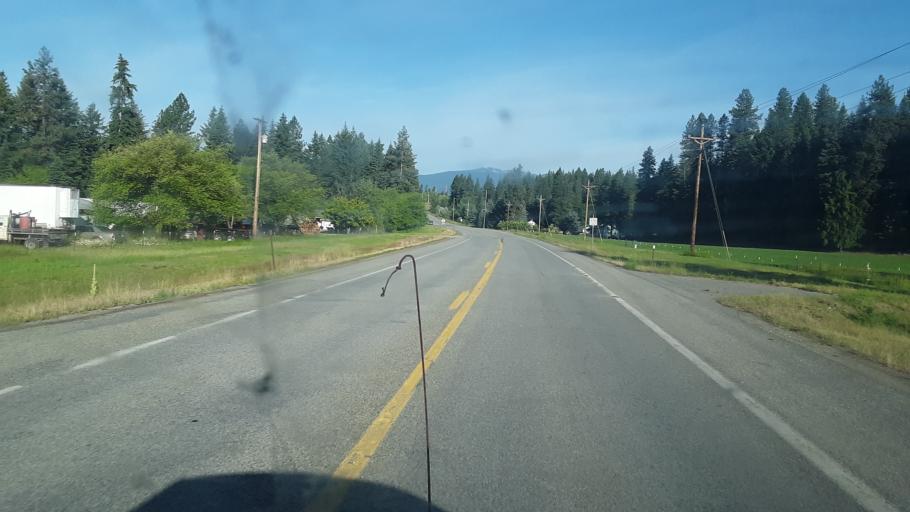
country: US
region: Idaho
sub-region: Boundary County
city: Bonners Ferry
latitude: 48.7313
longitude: -116.2442
